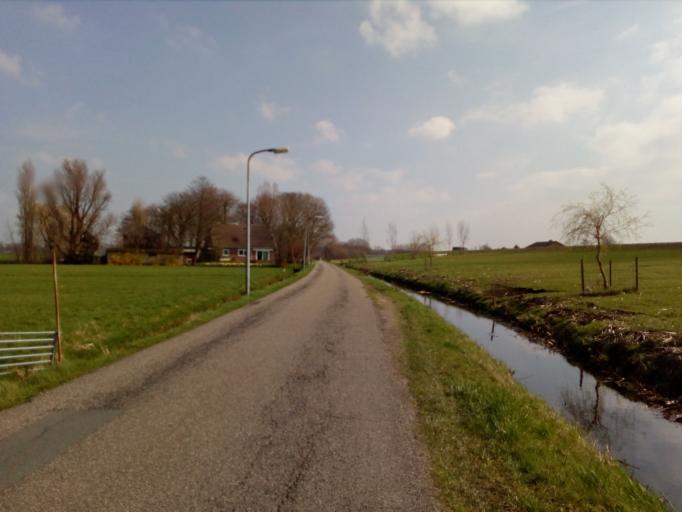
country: NL
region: South Holland
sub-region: Gemeente Zoetermeer
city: Zoetermeer
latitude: 52.0904
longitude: 4.4876
